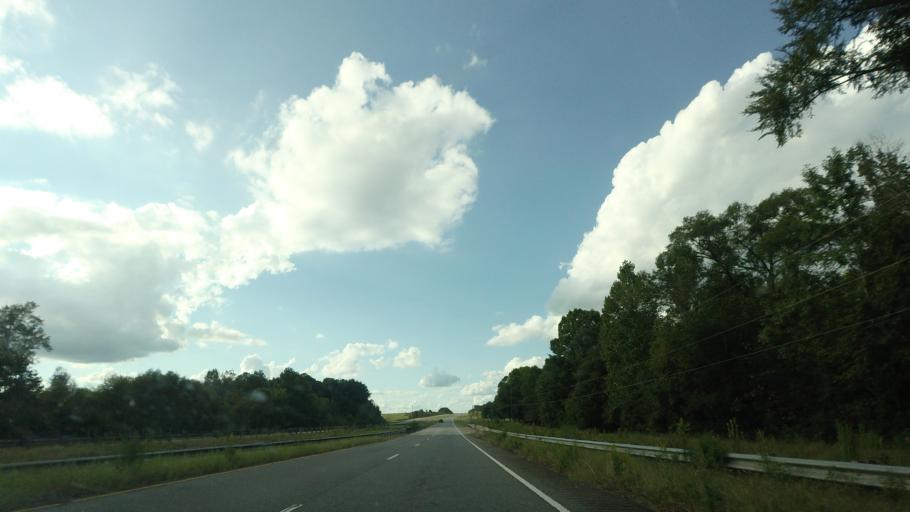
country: US
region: Georgia
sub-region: Houston County
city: Perry
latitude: 32.4264
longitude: -83.7135
